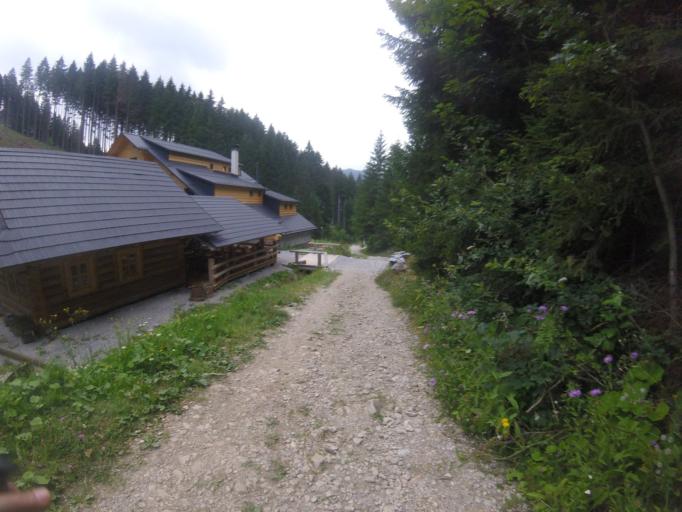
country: SK
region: Zilinsky
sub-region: Okres Zilina
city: Terchova
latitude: 49.2316
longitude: 19.0682
